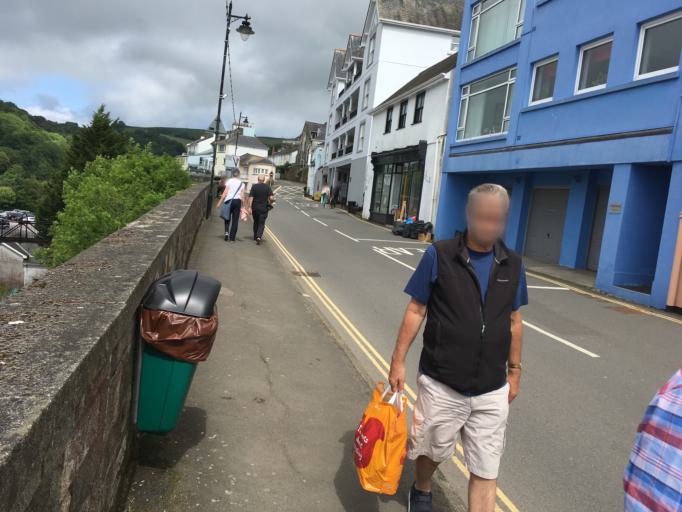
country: GB
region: England
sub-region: Devon
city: Dartmouth
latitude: 50.3493
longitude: -3.5711
